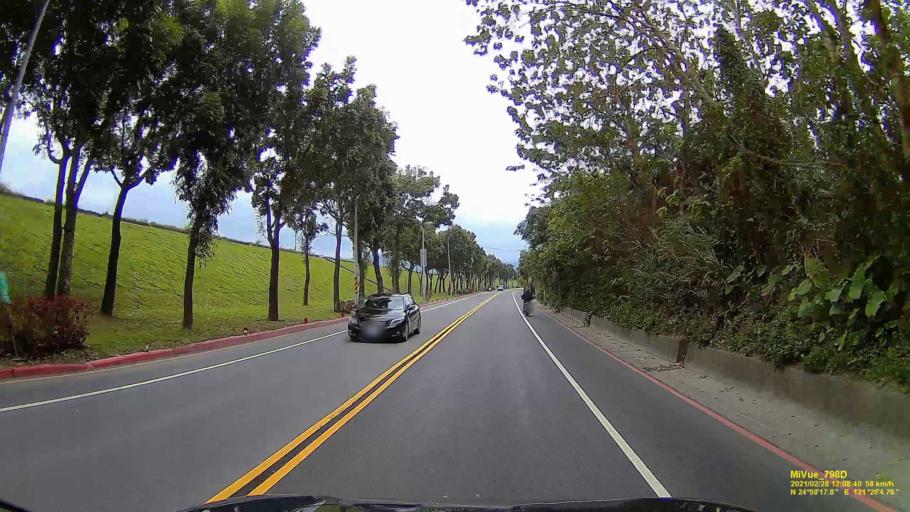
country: TW
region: Taipei
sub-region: Taipei
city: Banqiao
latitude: 24.9881
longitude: 121.4346
